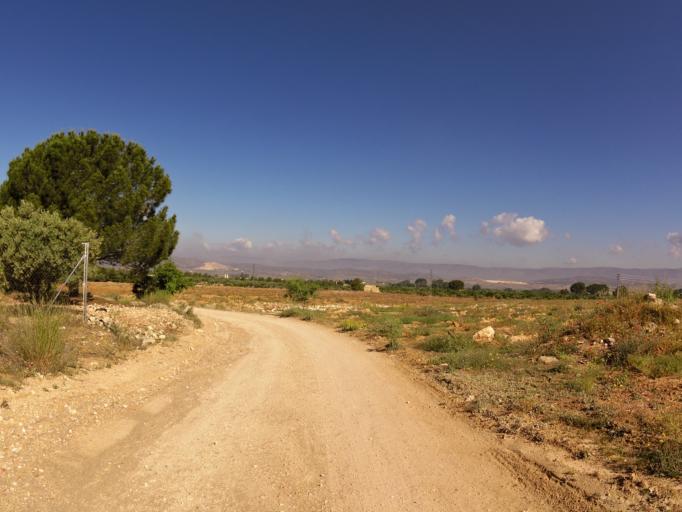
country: ES
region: Valencia
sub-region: Provincia de Alicante
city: Biar
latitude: 38.6394
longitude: -0.7697
